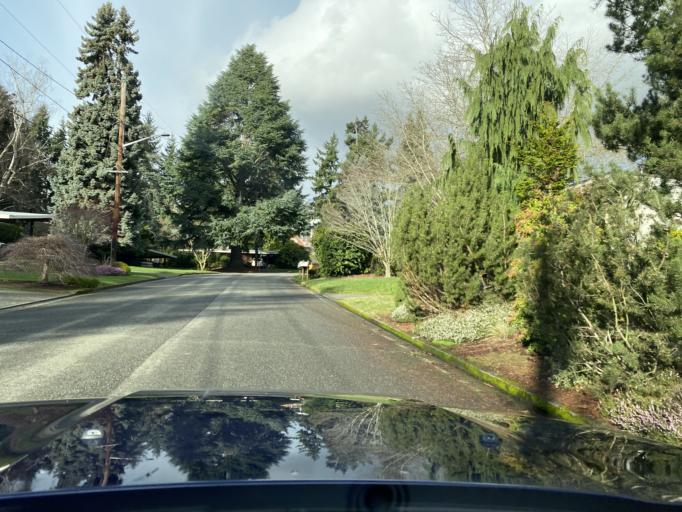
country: US
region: Washington
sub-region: King County
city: Bellevue
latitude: 47.6087
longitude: -122.1951
